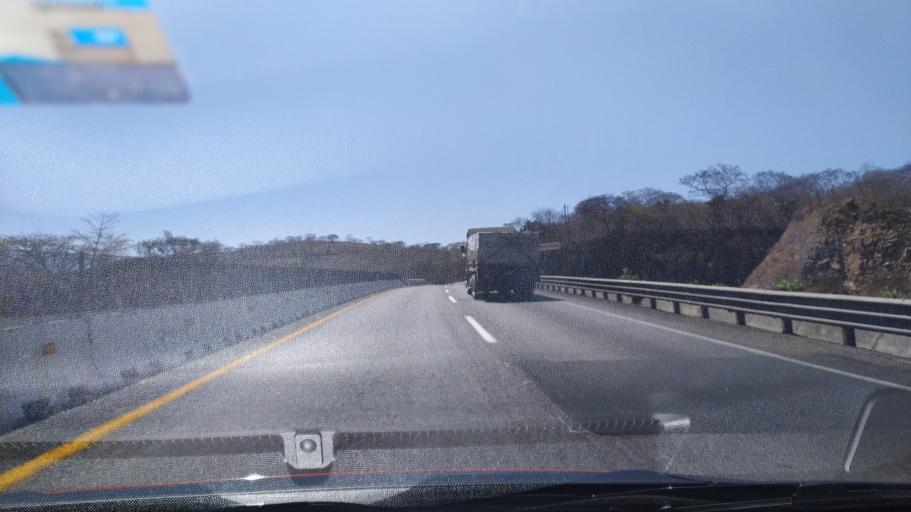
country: MX
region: Jalisco
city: Usmajac
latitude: 19.8541
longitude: -103.5066
